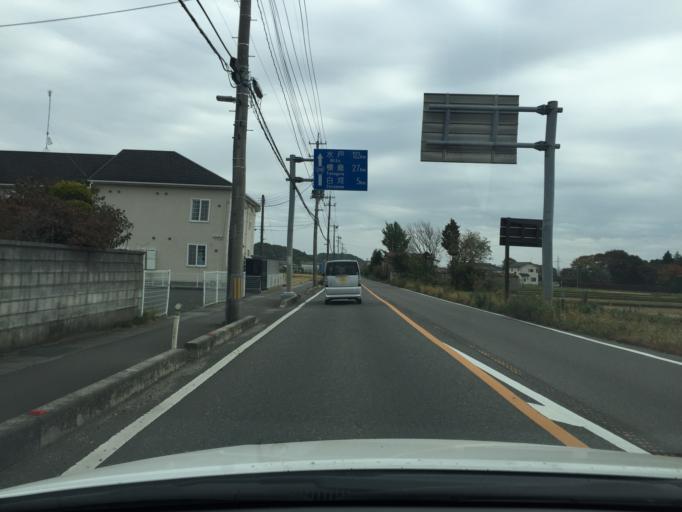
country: JP
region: Tochigi
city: Kuroiso
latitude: 37.1374
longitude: 140.1594
